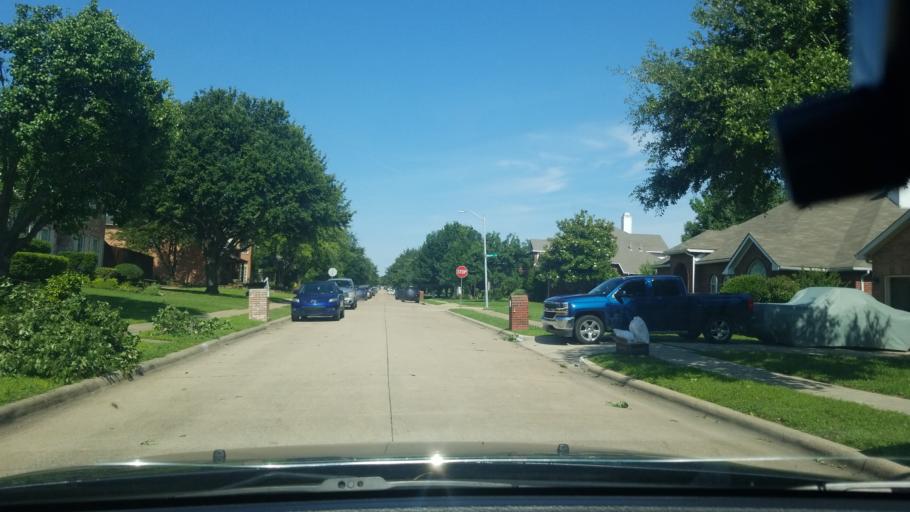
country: US
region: Texas
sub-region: Dallas County
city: Mesquite
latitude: 32.7759
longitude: -96.5820
